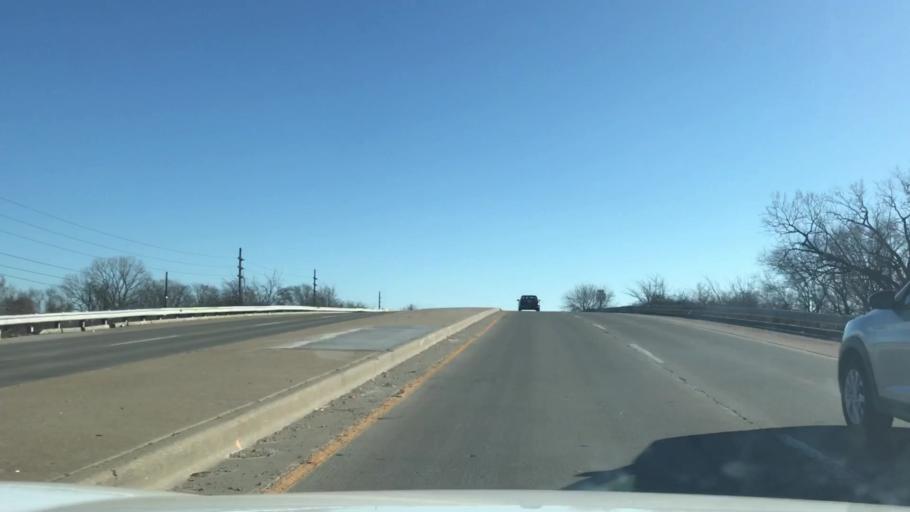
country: US
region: Illinois
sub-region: Saint Clair County
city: Alorton
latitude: 38.5945
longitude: -90.1217
